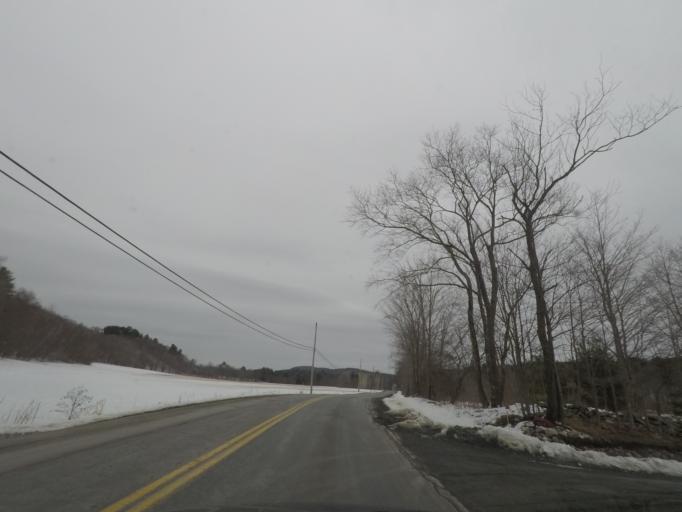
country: US
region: Massachusetts
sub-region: Berkshire County
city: Lanesborough
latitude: 42.5831
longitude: -73.3746
